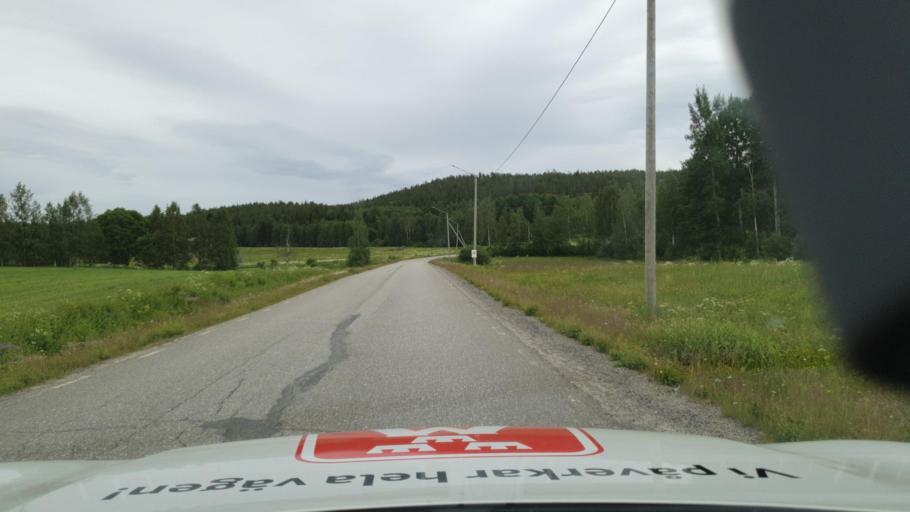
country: SE
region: Vaesterbotten
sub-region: Skelleftea Kommun
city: Burtraesk
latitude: 64.3092
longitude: 20.6547
